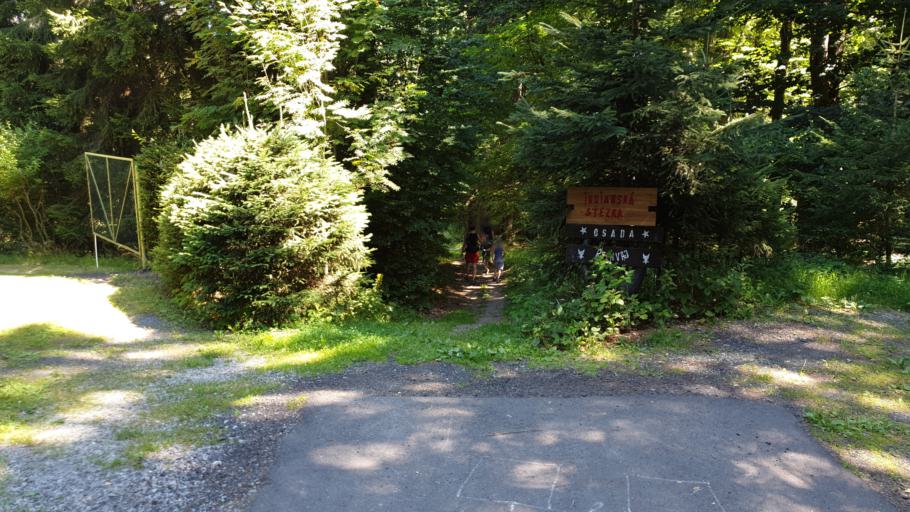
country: CZ
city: Novy Bor
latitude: 50.8090
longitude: 14.5505
